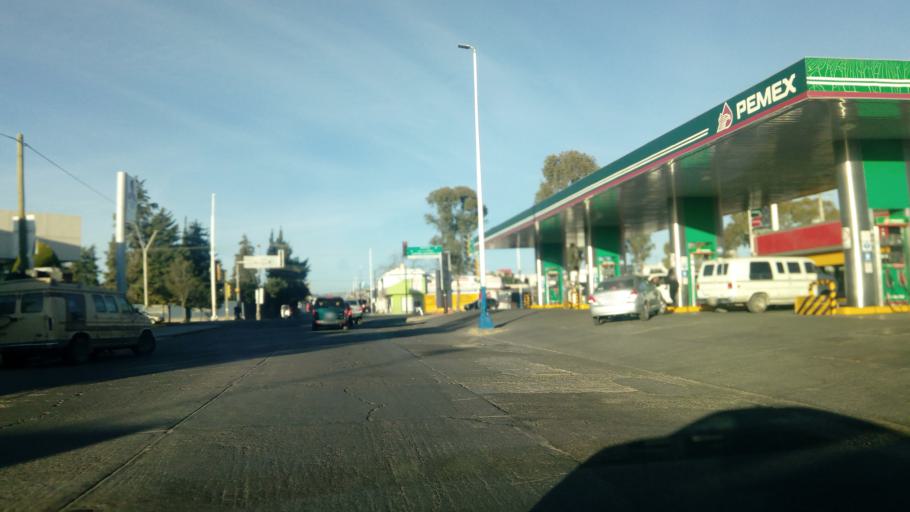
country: MX
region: Durango
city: Victoria de Durango
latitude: 24.0038
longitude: -104.6616
